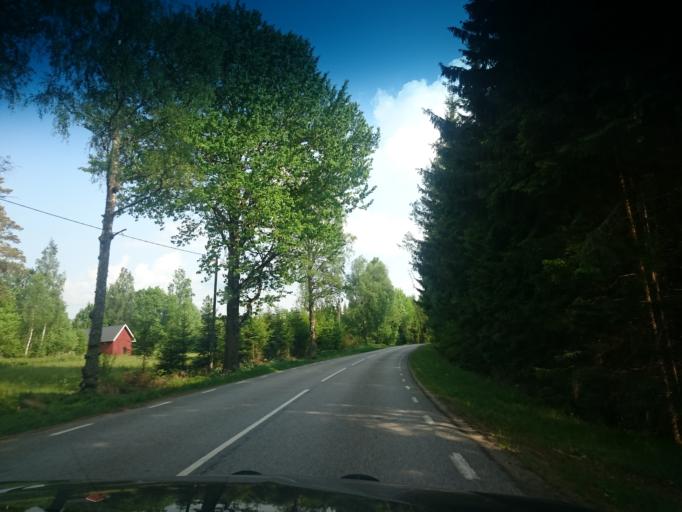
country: SE
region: Joenkoeping
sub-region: Vetlanda Kommun
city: Vetlanda
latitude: 57.3338
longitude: 15.0801
